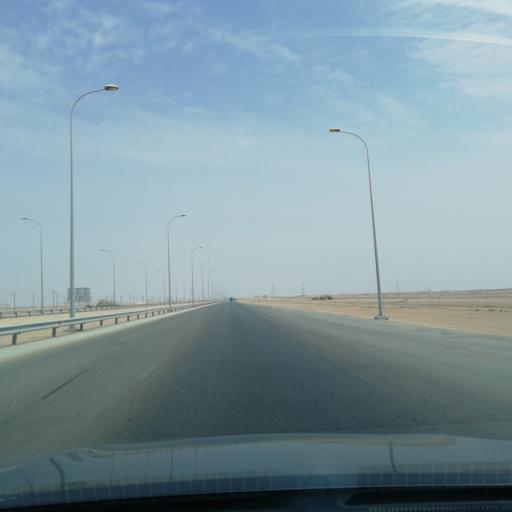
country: OM
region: Zufar
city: Salalah
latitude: 17.5779
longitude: 54.0440
